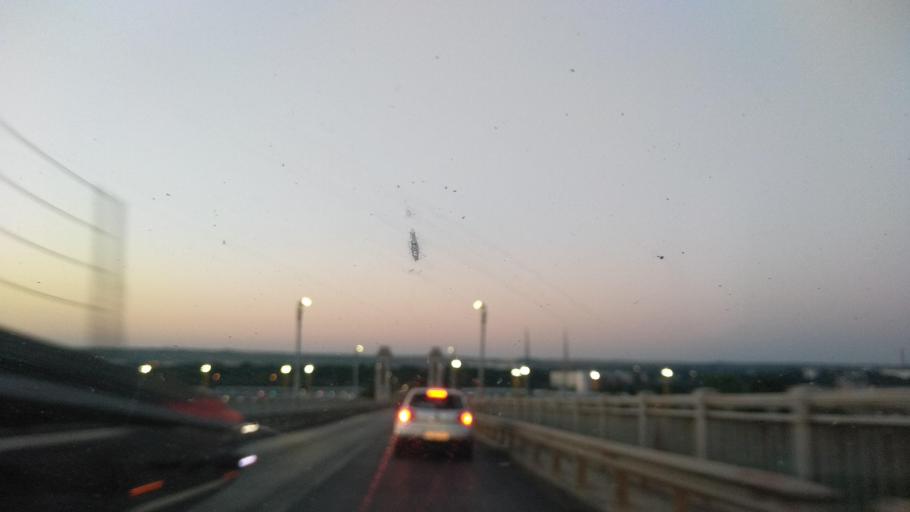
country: RO
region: Giurgiu
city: Giurgiu
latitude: 43.8822
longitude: 26.0124
